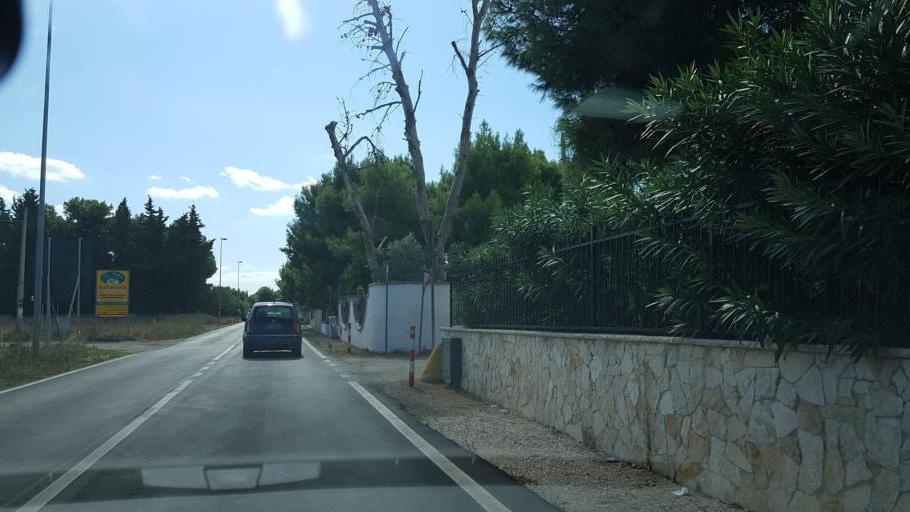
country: IT
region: Apulia
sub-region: Provincia di Lecce
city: Porto Cesareo
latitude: 40.2454
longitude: 17.9135
